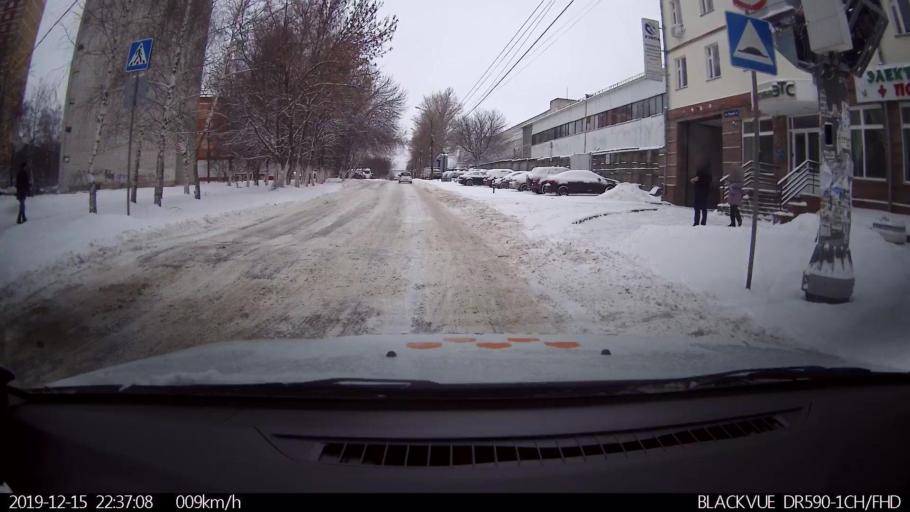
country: RU
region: Nizjnij Novgorod
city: Nizhniy Novgorod
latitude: 56.2383
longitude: 43.9710
